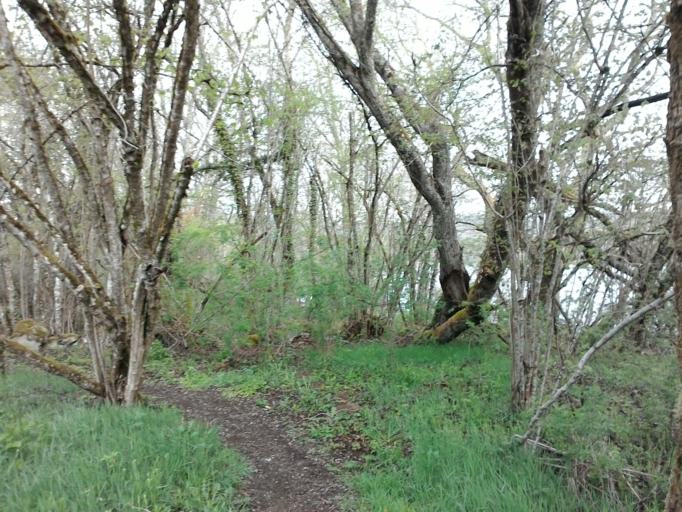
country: FR
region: Bourgogne
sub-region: Departement de la Cote-d'Or
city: Saulieu
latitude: 47.2507
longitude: 4.2039
